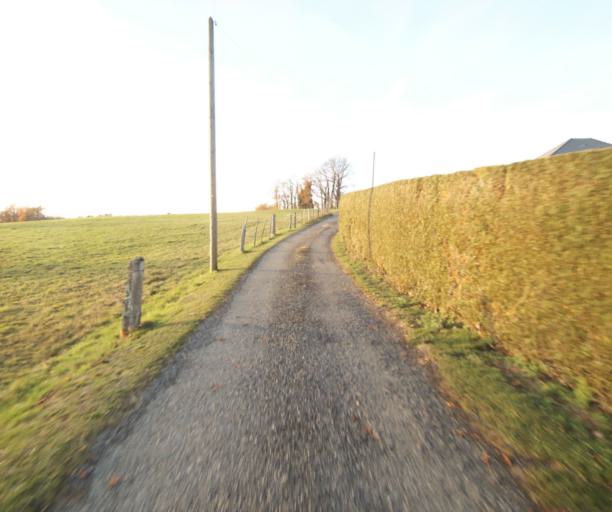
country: FR
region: Limousin
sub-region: Departement de la Correze
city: Laguenne
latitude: 45.2301
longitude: 1.8233
